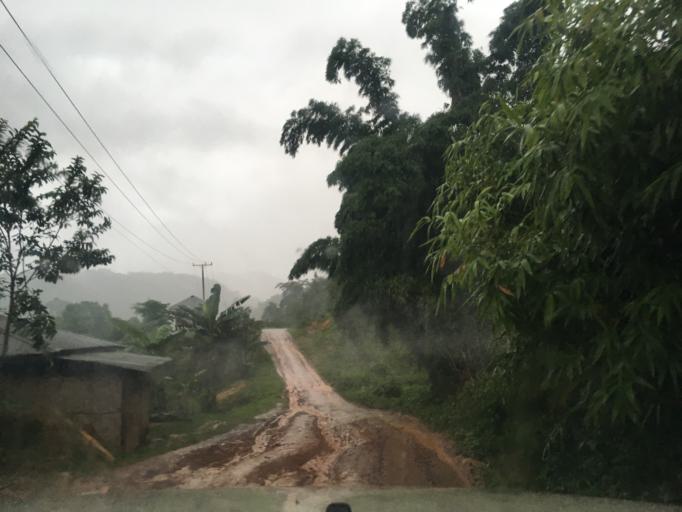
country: LA
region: Oudomxai
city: Muang La
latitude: 21.2400
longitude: 101.9539
